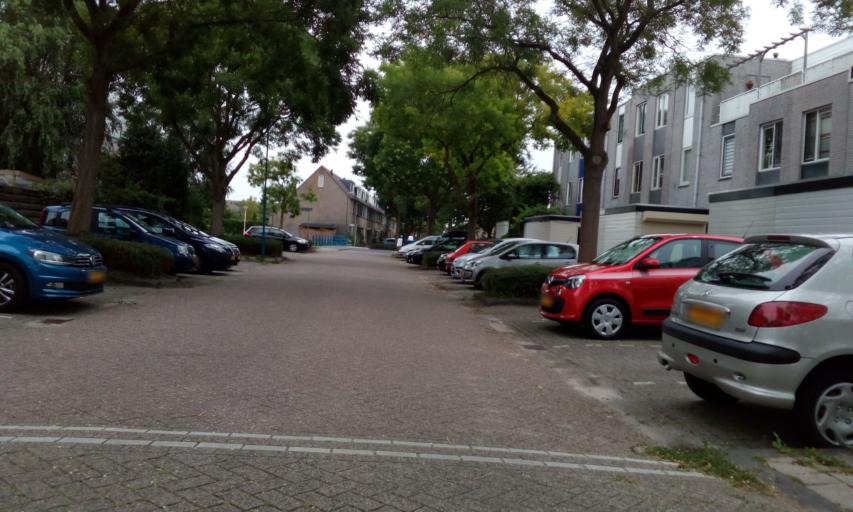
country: NL
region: South Holland
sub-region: Gemeente Zoetermeer
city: Zoetermeer
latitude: 52.0382
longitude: 4.4973
